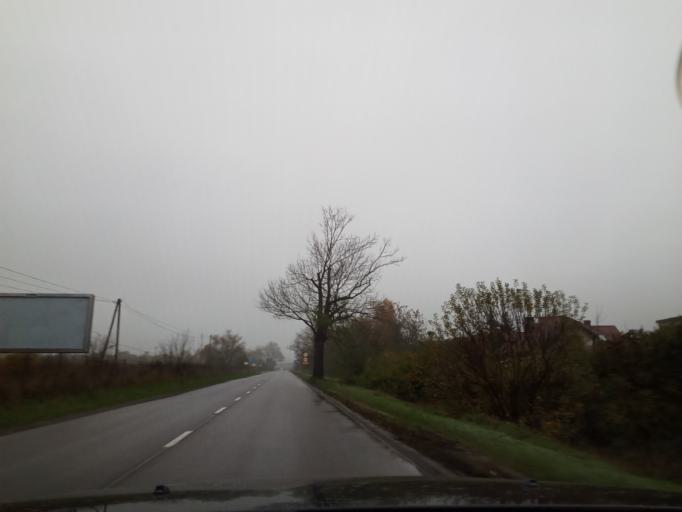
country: PL
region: Lesser Poland Voivodeship
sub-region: Powiat wielicki
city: Kokotow
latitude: 50.1026
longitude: 20.0708
